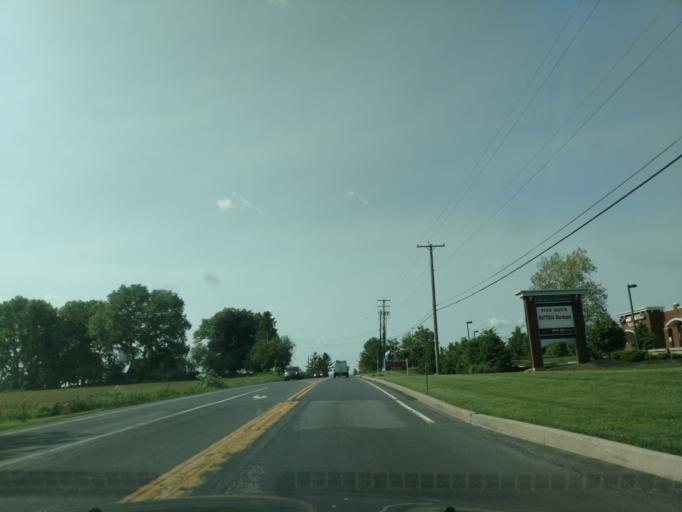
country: US
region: Pennsylvania
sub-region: Lebanon County
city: Lebanon South
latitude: 40.3058
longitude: -76.4241
